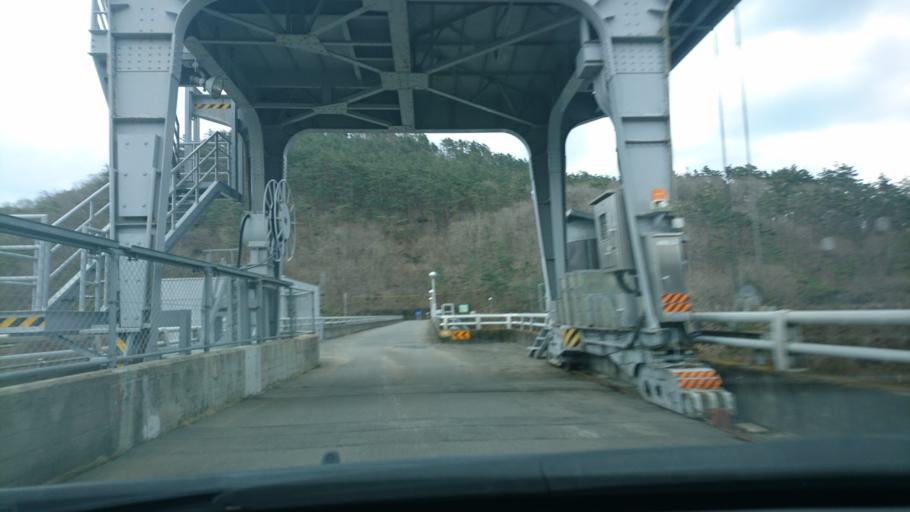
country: JP
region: Iwate
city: Hanamaki
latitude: 39.3429
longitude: 141.3187
